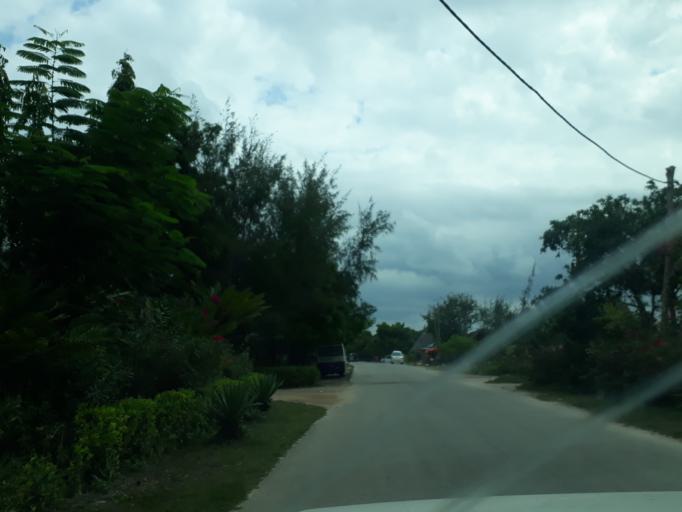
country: TZ
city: Kiwengwa
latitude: -6.0881
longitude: 39.4241
